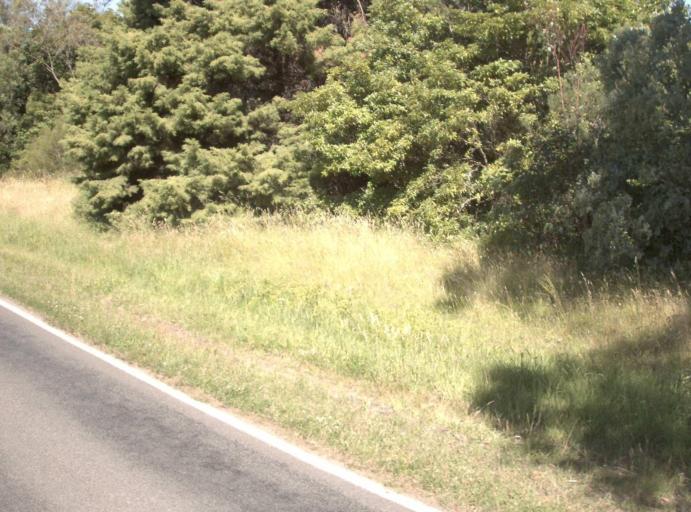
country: AU
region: Victoria
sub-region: Latrobe
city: Morwell
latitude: -38.6425
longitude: 146.4839
